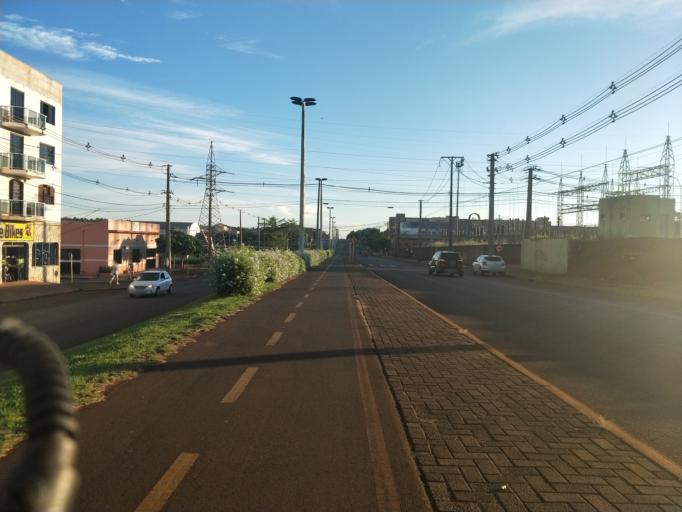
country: BR
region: Parana
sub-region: Marechal Candido Rondon
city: Marechal Candido Rondon
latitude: -24.5546
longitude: -54.0471
